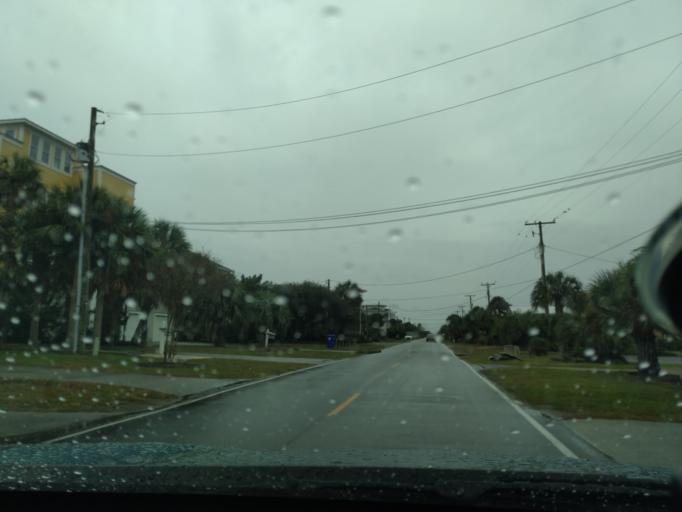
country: US
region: South Carolina
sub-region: Charleston County
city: Folly Beach
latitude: 32.6783
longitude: -79.8962
